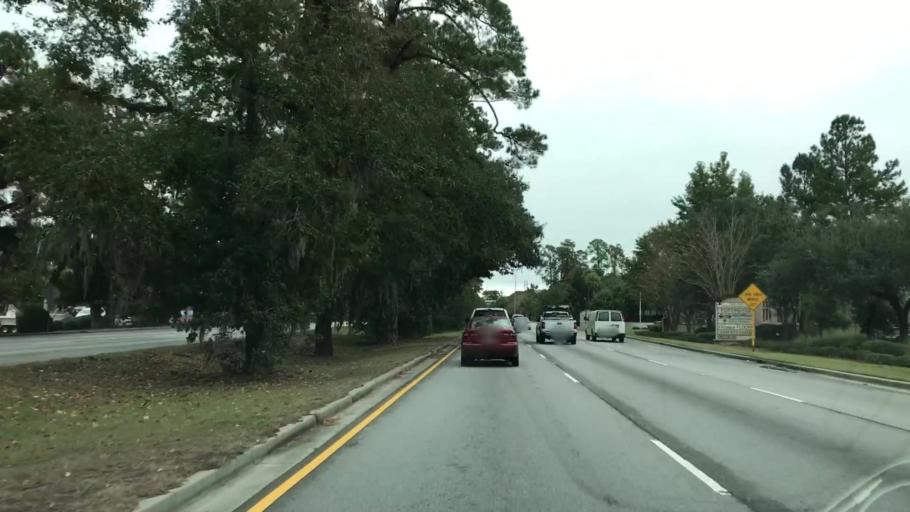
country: US
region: South Carolina
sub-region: Beaufort County
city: Bluffton
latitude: 32.2371
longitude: -80.8089
